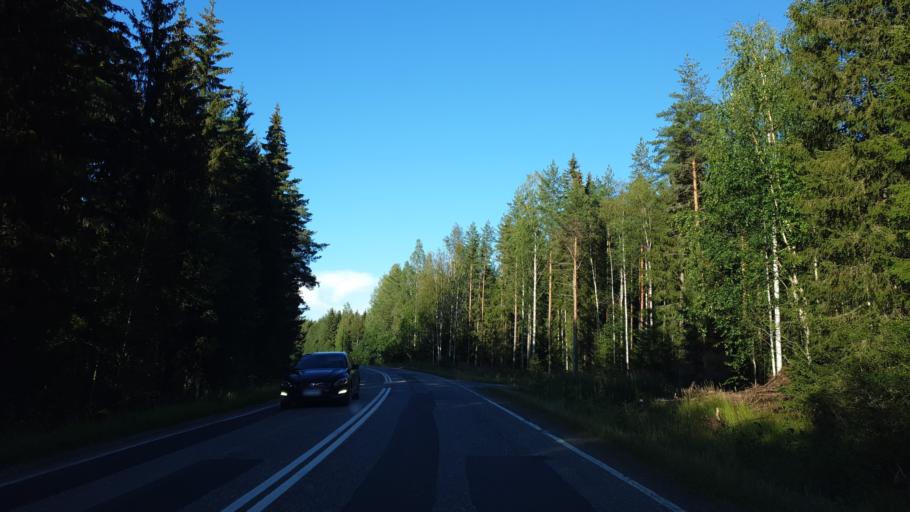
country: FI
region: Northern Savo
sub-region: Koillis-Savo
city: Juankoski
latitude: 63.0915
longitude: 28.4139
